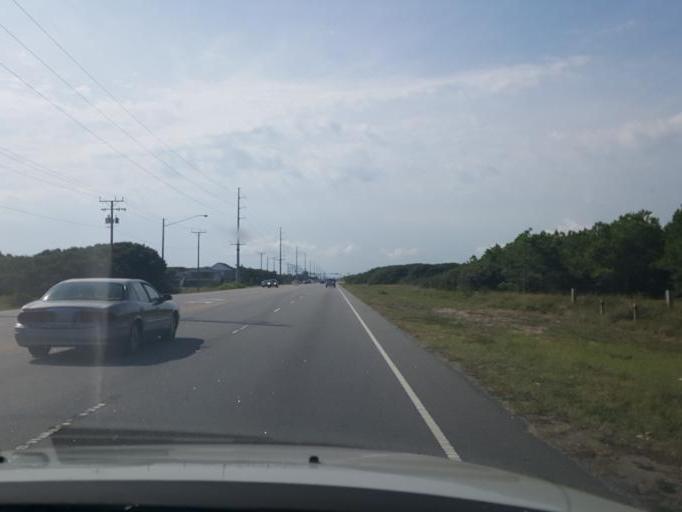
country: US
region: North Carolina
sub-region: Dare County
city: Kill Devil Hills
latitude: 36.0249
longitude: -75.6678
